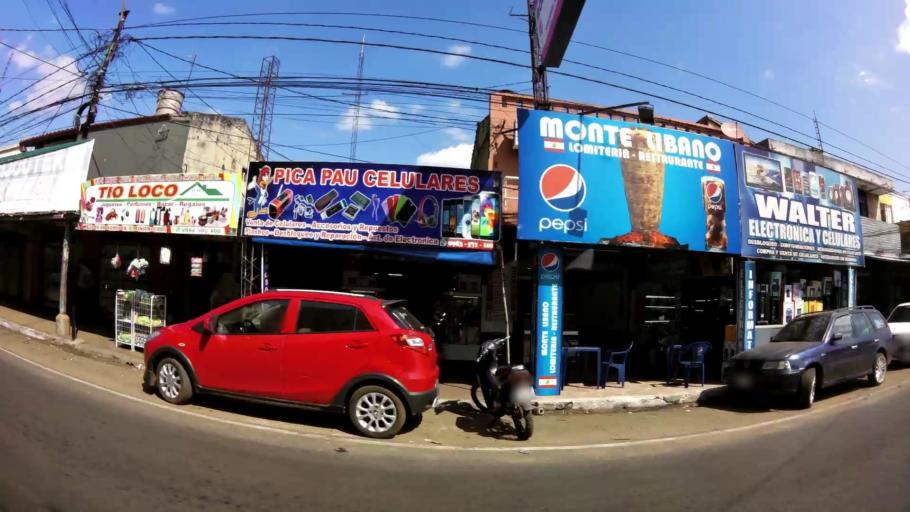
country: PY
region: Central
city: San Lorenzo
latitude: -25.3472
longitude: -57.5123
